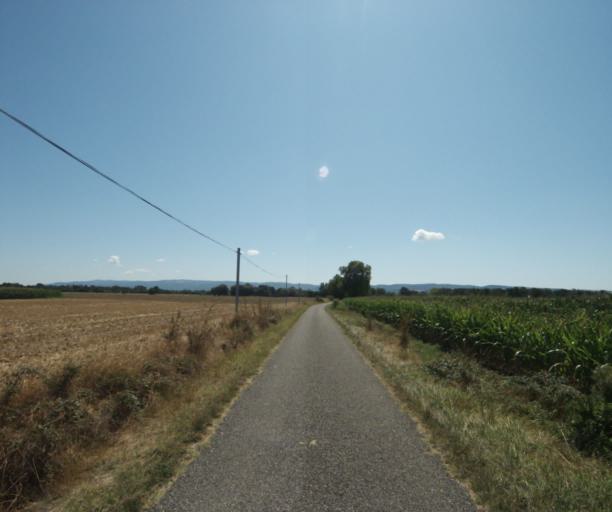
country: FR
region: Midi-Pyrenees
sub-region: Departement de la Haute-Garonne
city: Revel
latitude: 43.4866
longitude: 1.9638
